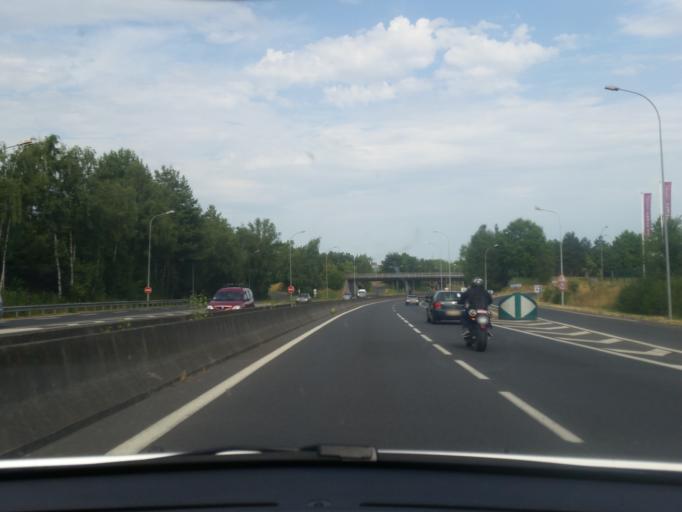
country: FR
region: Pays de la Loire
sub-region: Departement de Maine-et-Loire
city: Avrille
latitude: 47.4695
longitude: -0.5939
